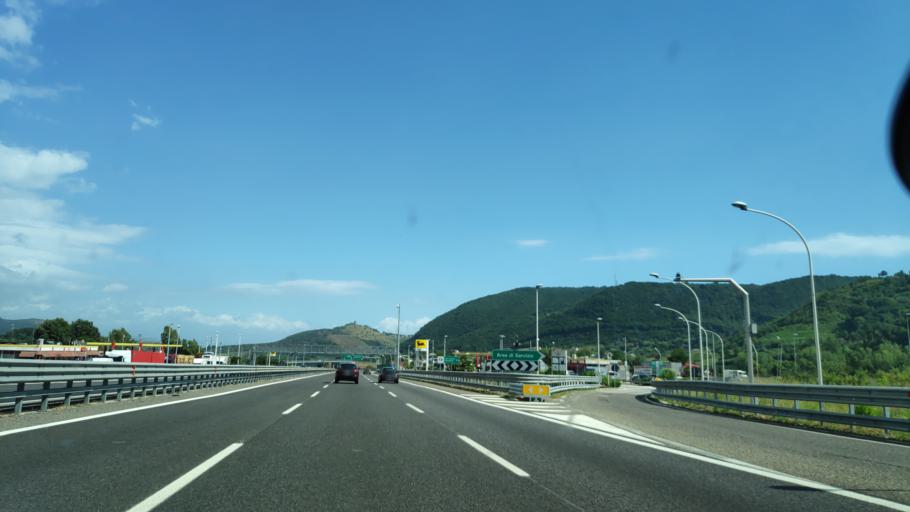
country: IT
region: Campania
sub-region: Provincia di Salerno
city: San Mango Piemonte
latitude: 40.6940
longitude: 14.8334
